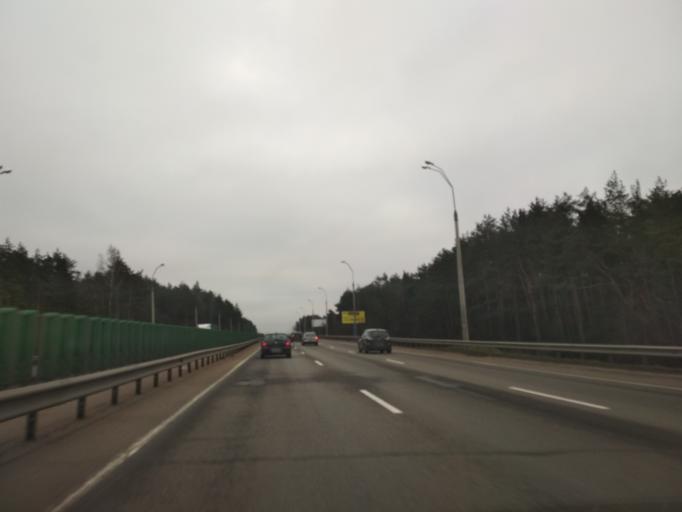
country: BY
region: Minsk
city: Vyaliki Trastsyanets
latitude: 53.8314
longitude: 27.7400
